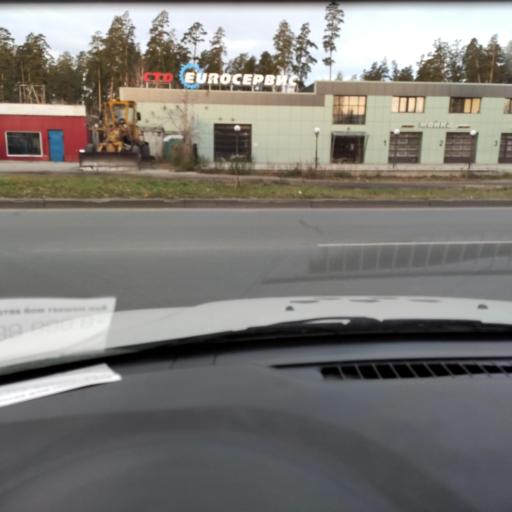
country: RU
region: Samara
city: Tol'yatti
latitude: 53.5075
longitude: 49.3912
